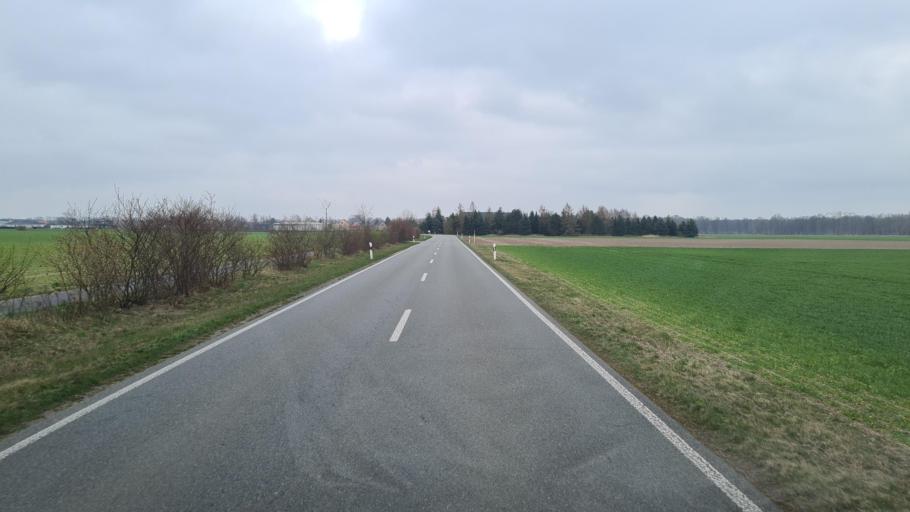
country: DE
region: Saxony
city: Nauwalde
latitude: 51.3972
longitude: 13.4589
